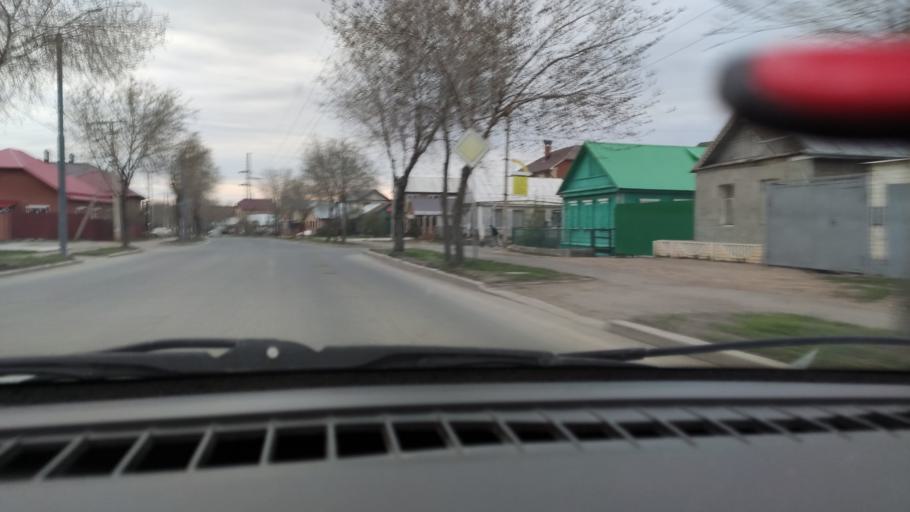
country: RU
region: Orenburg
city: Orenburg
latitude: 51.7785
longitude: 55.1152
